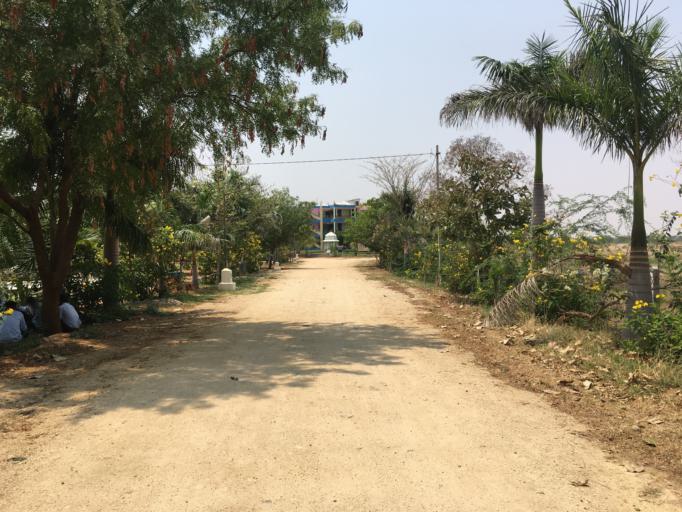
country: IN
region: Andhra Pradesh
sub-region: Anantapur
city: Puttaparthi
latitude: 14.1375
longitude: 77.7800
